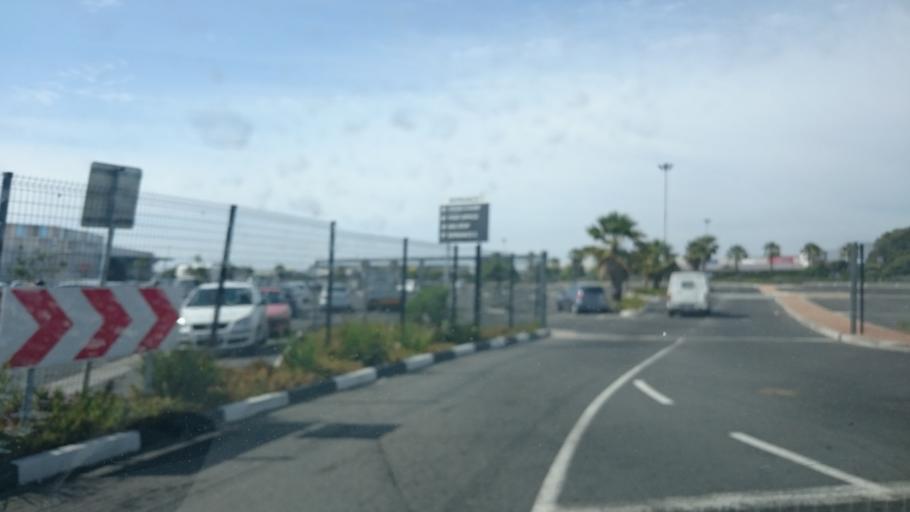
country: ZA
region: Western Cape
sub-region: City of Cape Town
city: Lansdowne
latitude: -34.0186
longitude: 18.5160
